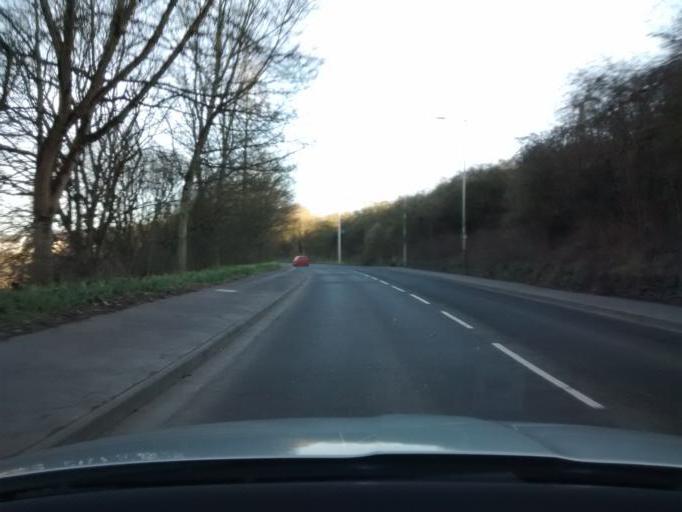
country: GB
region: Scotland
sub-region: Perth and Kinross
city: Perth
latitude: 56.3751
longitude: -3.4284
